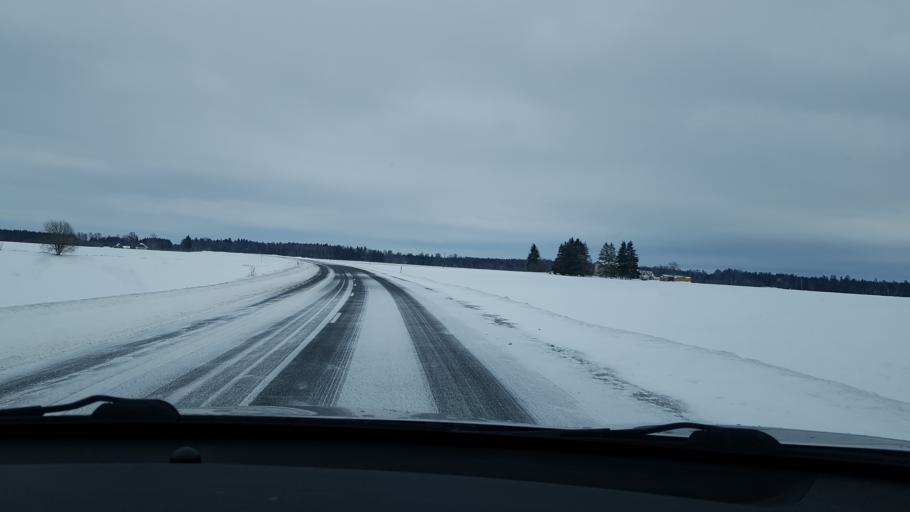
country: EE
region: Jaervamaa
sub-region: Jaerva-Jaani vald
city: Jarva-Jaani
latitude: 59.1121
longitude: 25.7961
